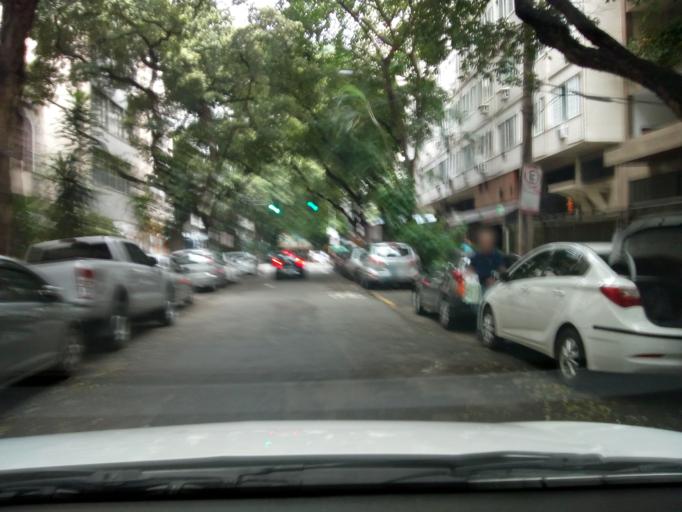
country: BR
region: Rio de Janeiro
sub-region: Rio De Janeiro
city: Rio de Janeiro
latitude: -22.9678
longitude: -43.1831
